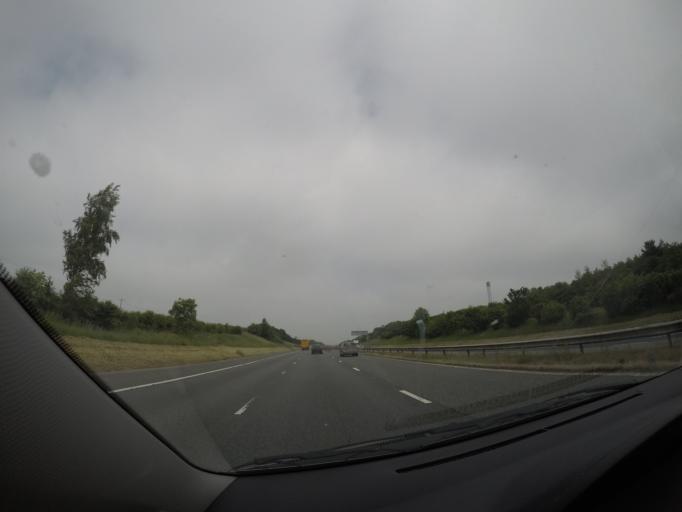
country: GB
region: England
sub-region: North Yorkshire
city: Boroughbridge
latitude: 54.0296
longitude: -1.3850
